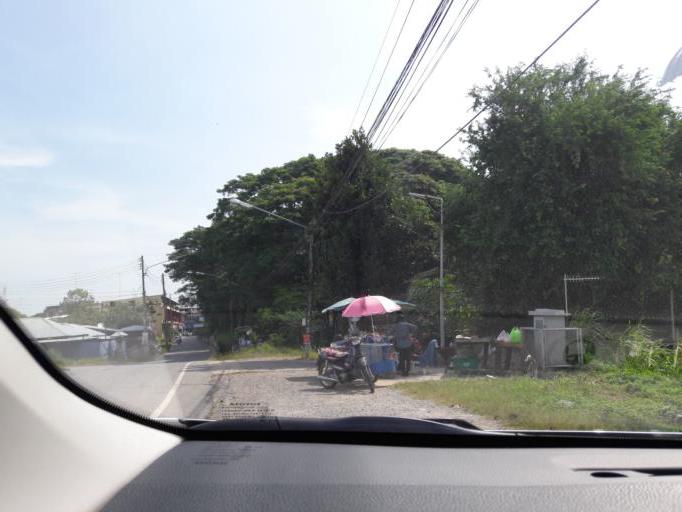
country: TH
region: Ang Thong
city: Ang Thong
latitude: 14.5898
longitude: 100.4483
